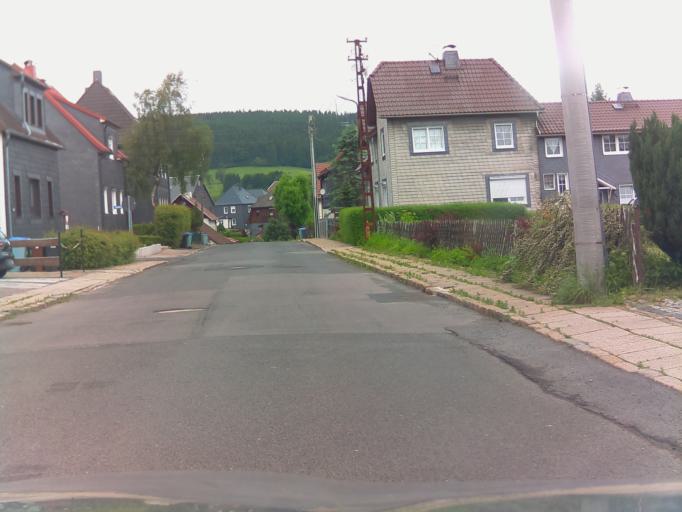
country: DE
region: Thuringia
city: Schmiedefeld am Rennsteig
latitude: 50.6053
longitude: 10.8133
